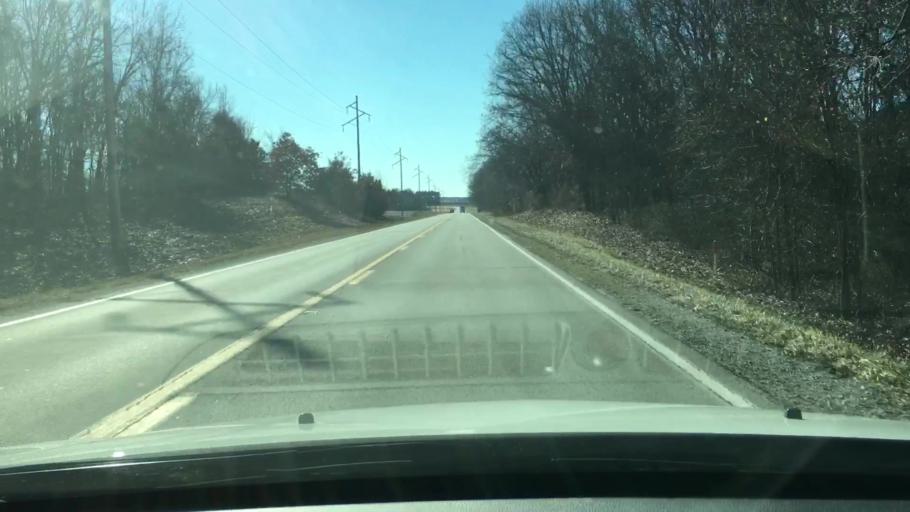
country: US
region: Illinois
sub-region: Morgan County
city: Meredosia
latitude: 39.8954
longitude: -90.4987
